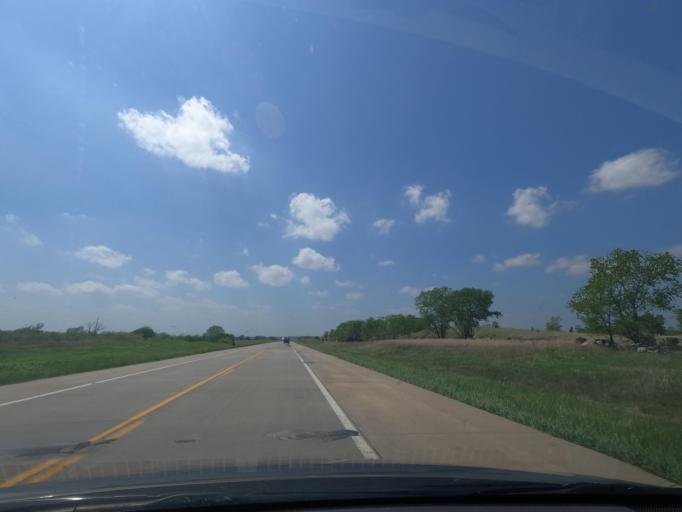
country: US
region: Kansas
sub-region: Wilson County
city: Fredonia
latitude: 37.6241
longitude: -96.0571
